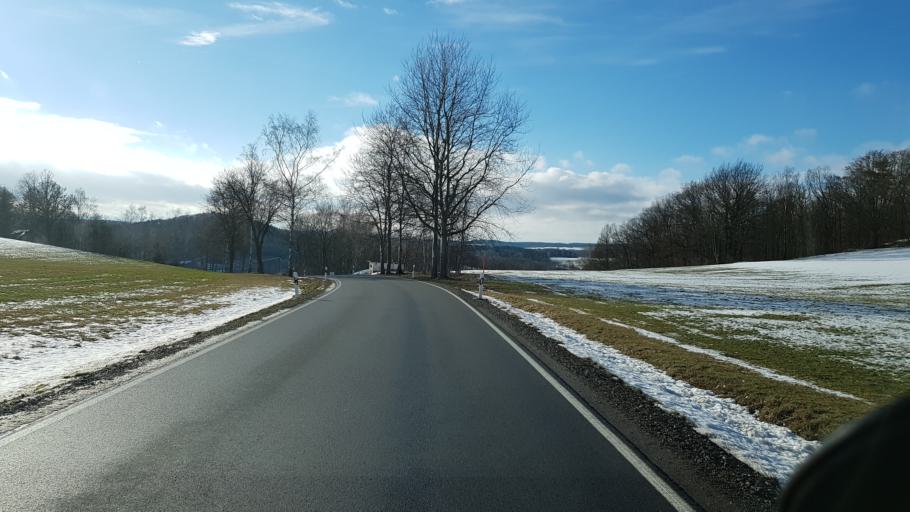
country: DE
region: Saxony
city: Kirchberg
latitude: 50.6354
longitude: 12.5305
